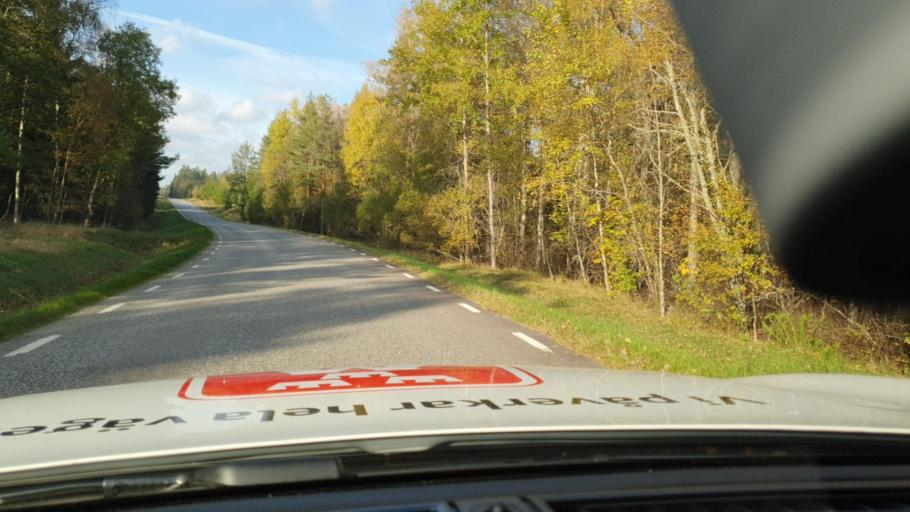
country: SE
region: Kronoberg
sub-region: Markaryds Kommun
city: Markaryd
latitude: 56.4977
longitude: 13.5274
